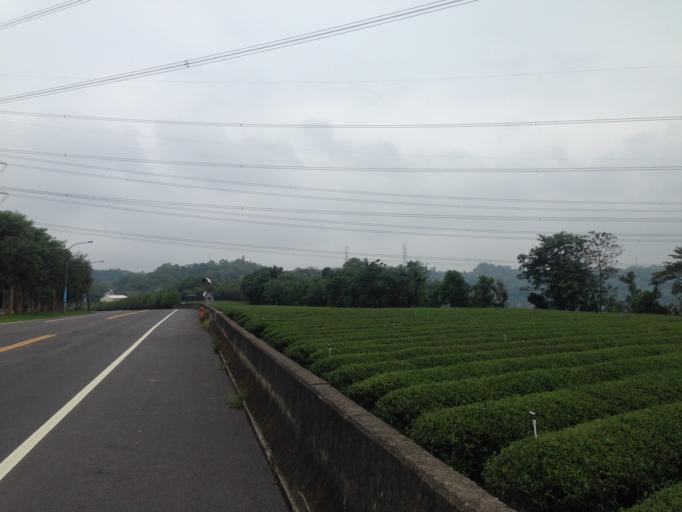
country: TW
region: Taiwan
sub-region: Hsinchu
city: Hsinchu
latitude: 24.6929
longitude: 120.9880
